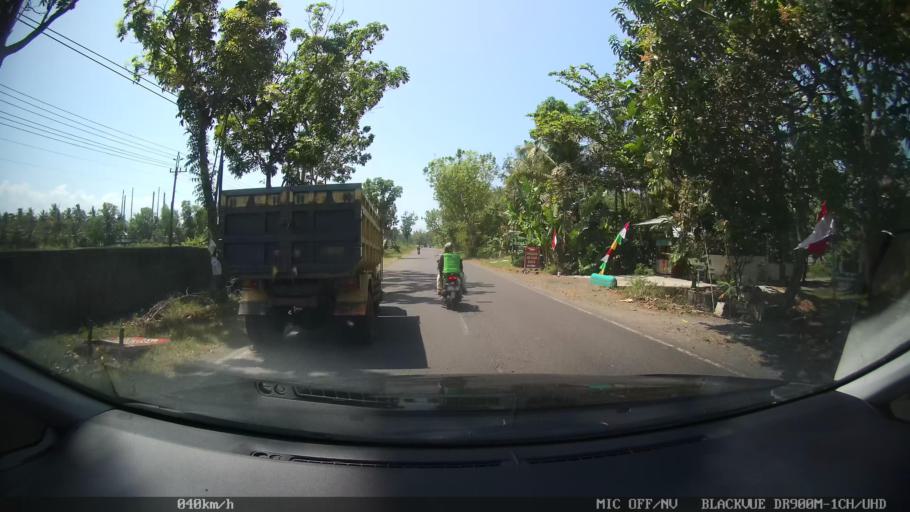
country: ID
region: Daerah Istimewa Yogyakarta
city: Srandakan
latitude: -7.9327
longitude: 110.1425
